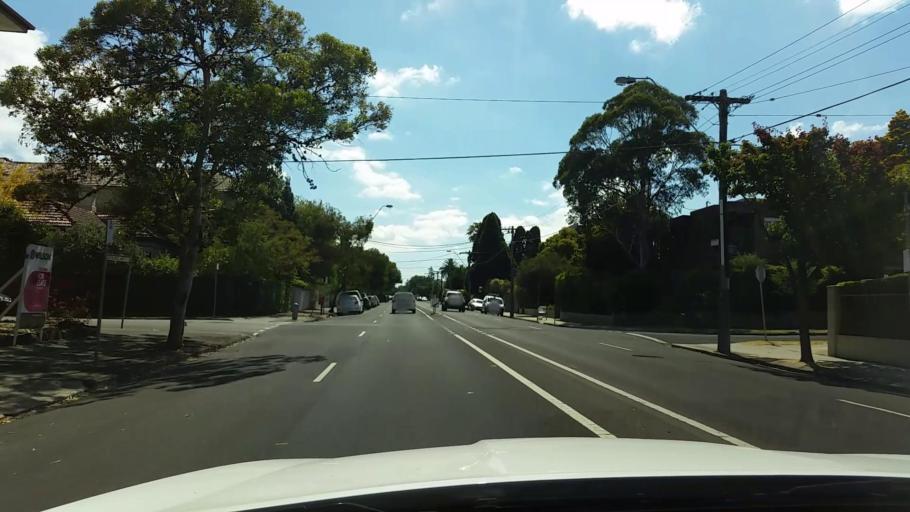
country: AU
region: Victoria
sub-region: Port Phillip
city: Balaclava
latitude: -37.8731
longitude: 144.9987
